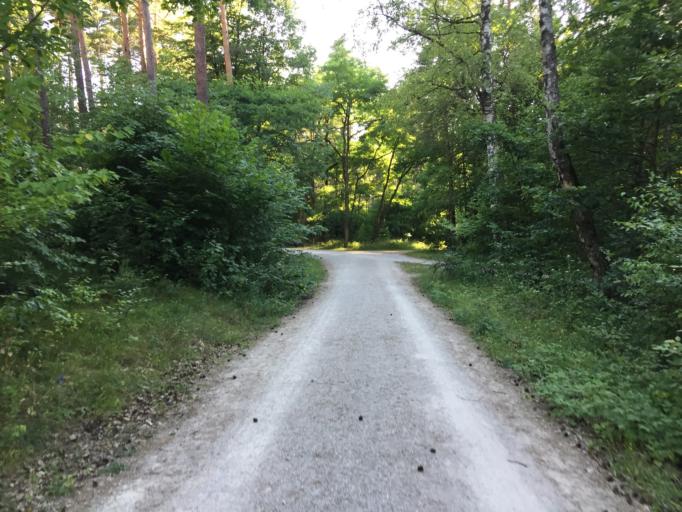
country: DE
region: Bavaria
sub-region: Regierungsbezirk Mittelfranken
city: Erlangen
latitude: 49.5695
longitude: 11.0158
